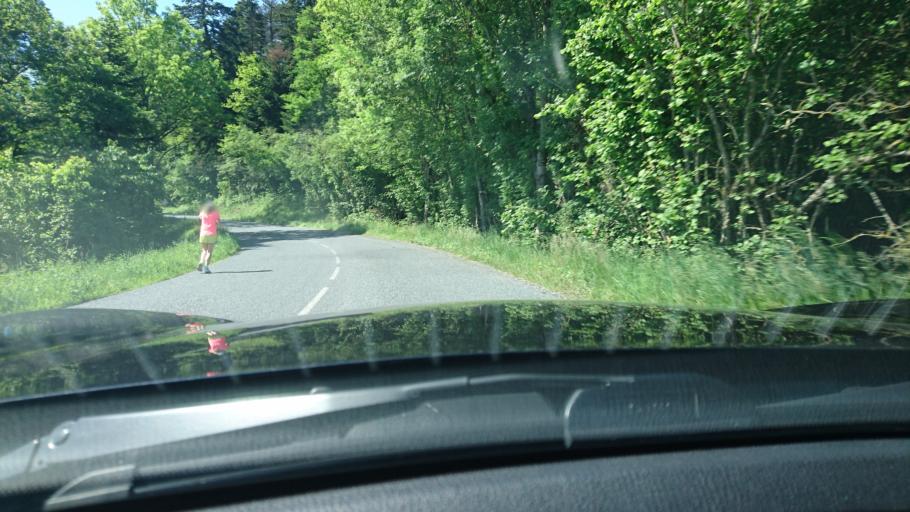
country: FR
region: Rhone-Alpes
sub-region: Departement du Rhone
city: Montrottier
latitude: 45.7972
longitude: 4.4503
